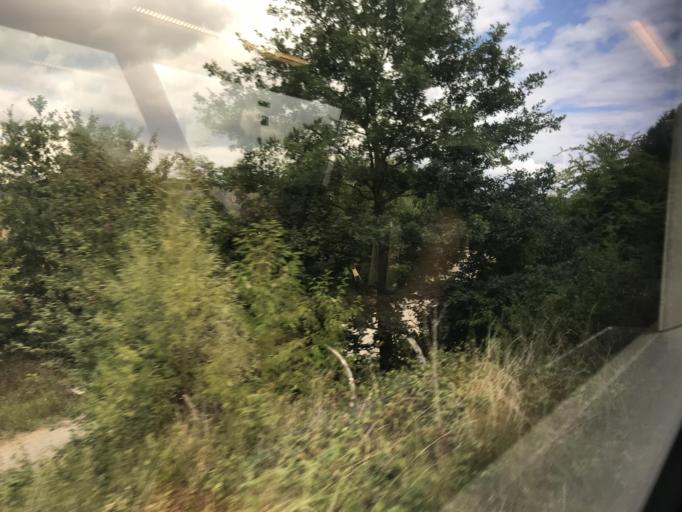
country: DE
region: Bavaria
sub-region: Regierungsbezirk Unterfranken
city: Fuchsstadt
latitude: 50.1289
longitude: 9.9454
